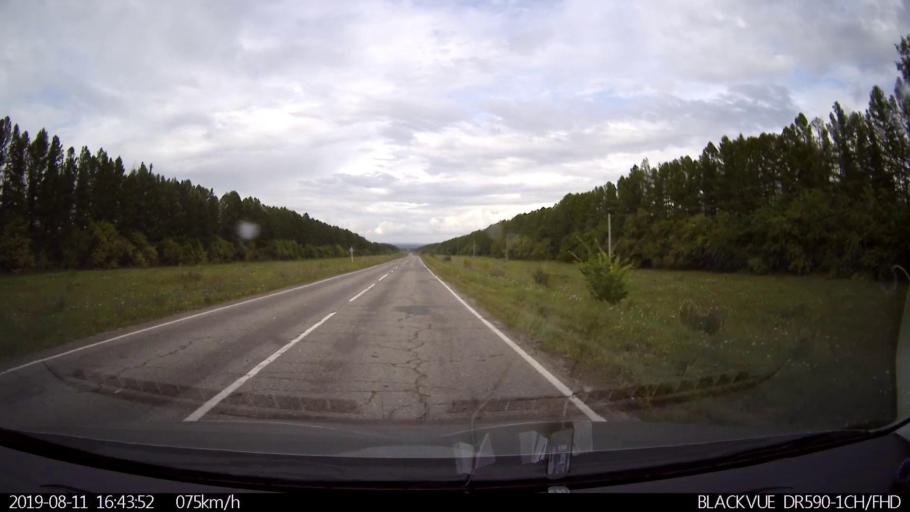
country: RU
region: Ulyanovsk
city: Mayna
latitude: 54.1730
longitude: 47.6762
